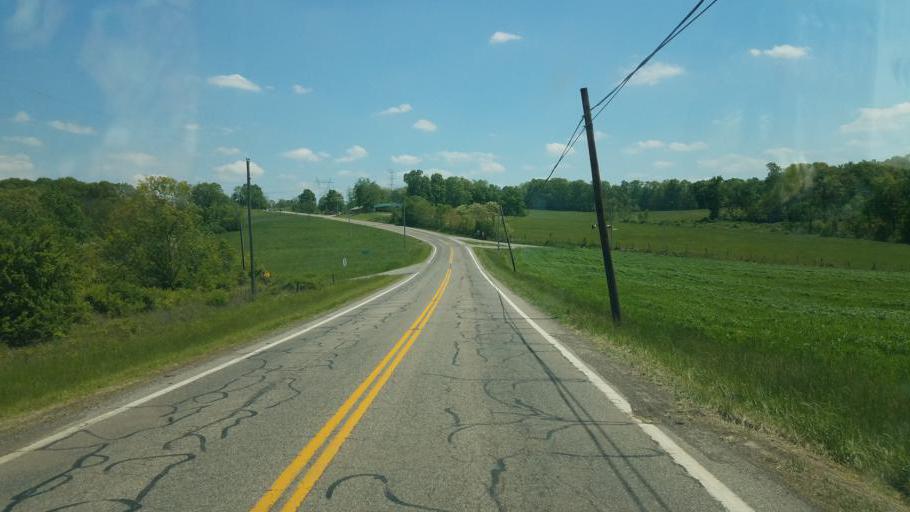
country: US
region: Ohio
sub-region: Muskingum County
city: Frazeysburg
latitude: 40.2146
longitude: -82.2578
